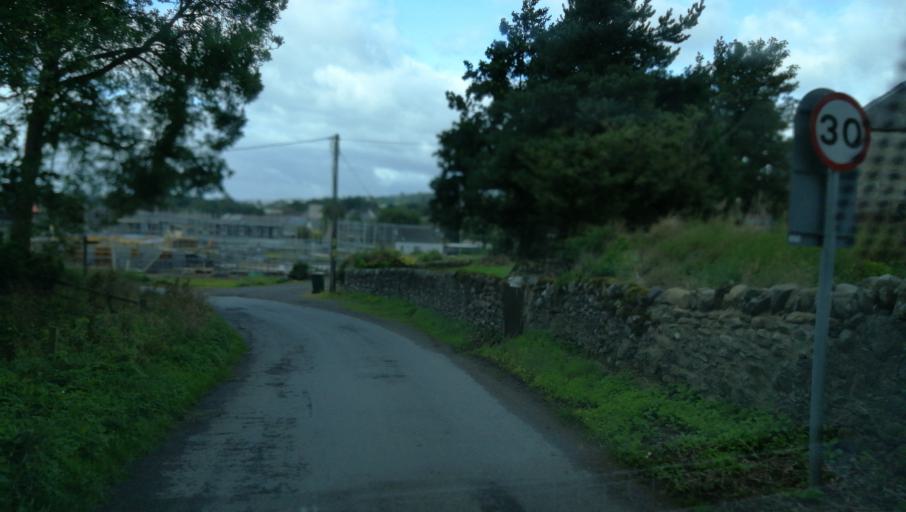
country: GB
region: Scotland
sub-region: Perth and Kinross
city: Blairgowrie
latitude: 56.5988
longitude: -3.3217
